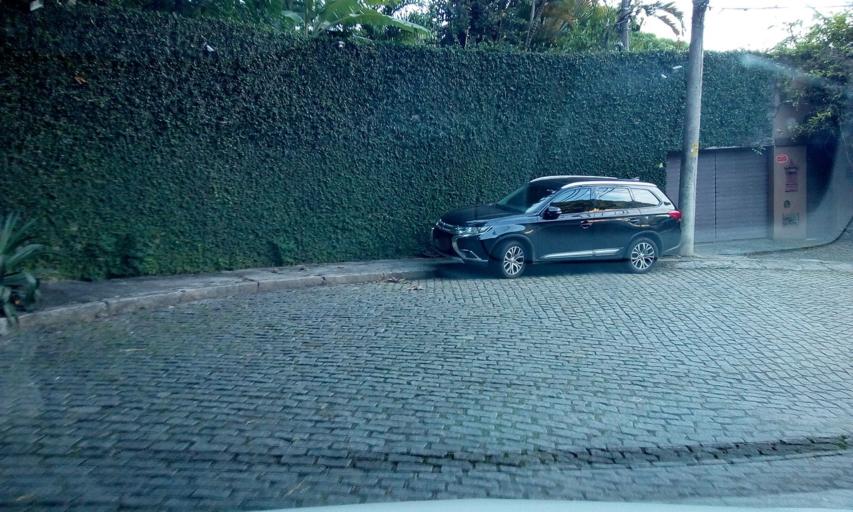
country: BR
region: Rio de Janeiro
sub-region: Rio De Janeiro
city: Rio de Janeiro
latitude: -22.9662
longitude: -43.1992
